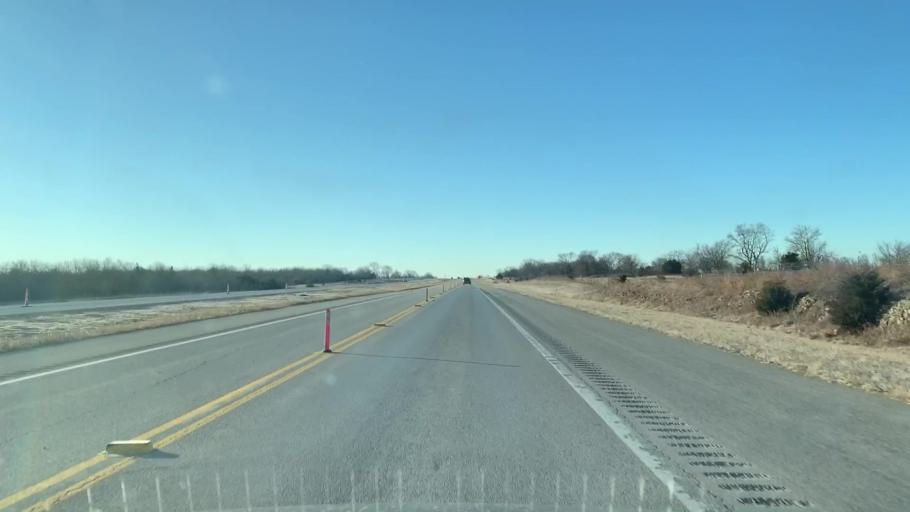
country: US
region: Kansas
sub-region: Bourbon County
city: Fort Scott
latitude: 37.7596
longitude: -94.7050
